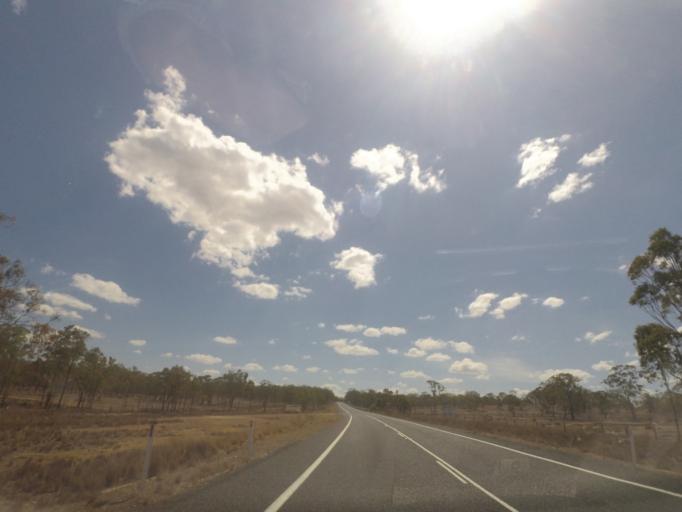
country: AU
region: Queensland
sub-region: Southern Downs
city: Warwick
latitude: -28.1610
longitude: 151.6892
